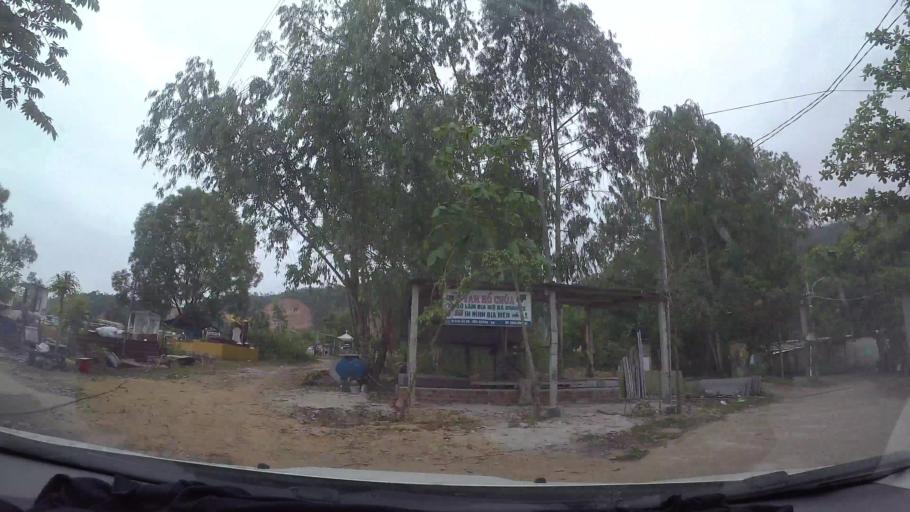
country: VN
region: Da Nang
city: Lien Chieu
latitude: 16.0709
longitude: 108.1374
